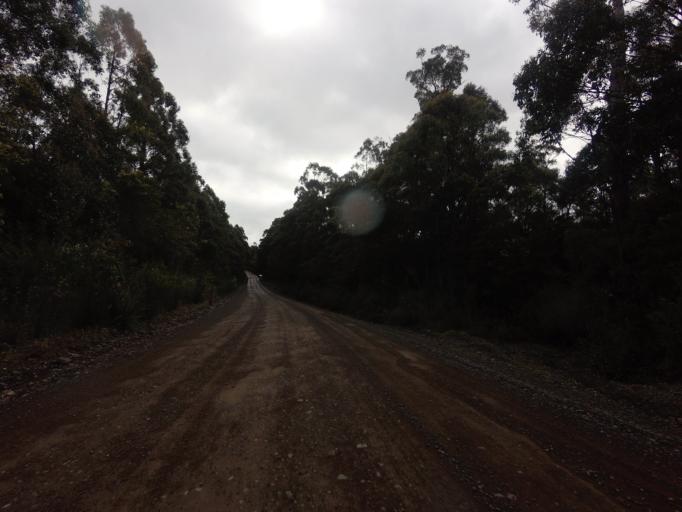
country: AU
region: Tasmania
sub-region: Huon Valley
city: Geeveston
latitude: -43.4669
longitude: 146.8994
